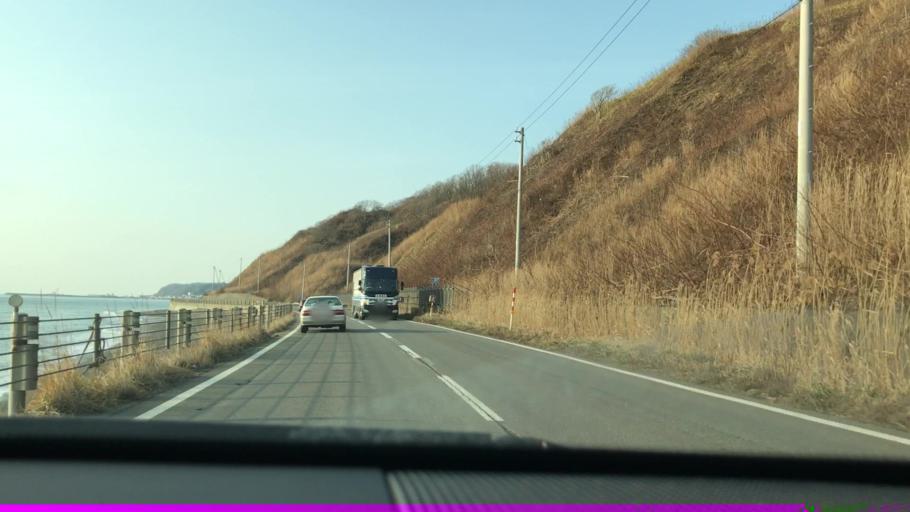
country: JP
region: Hokkaido
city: Shizunai-furukawacho
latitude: 42.2359
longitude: 142.5987
